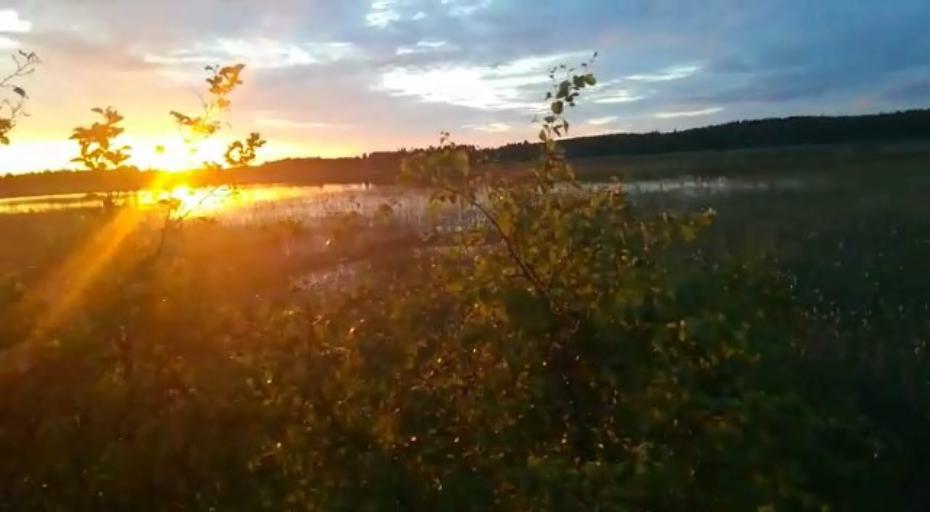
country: FI
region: Southern Savonia
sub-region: Savonlinna
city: Savonlinna
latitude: 61.9065
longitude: 28.9119
